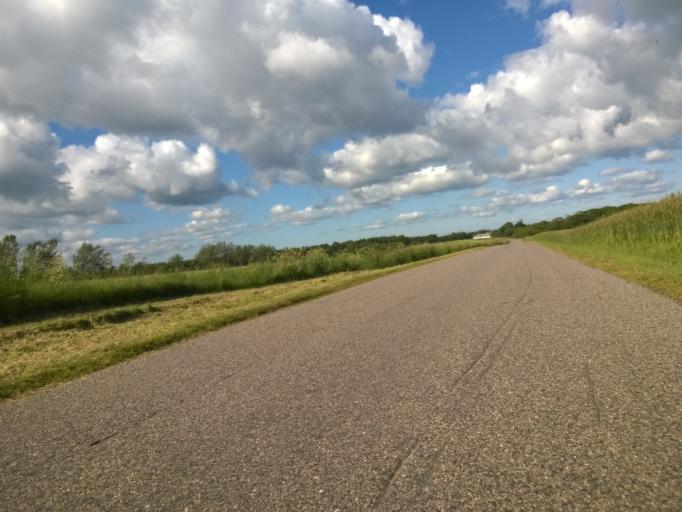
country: DK
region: Central Jutland
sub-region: Holstebro Kommune
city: Vinderup
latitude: 56.4744
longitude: 8.8586
